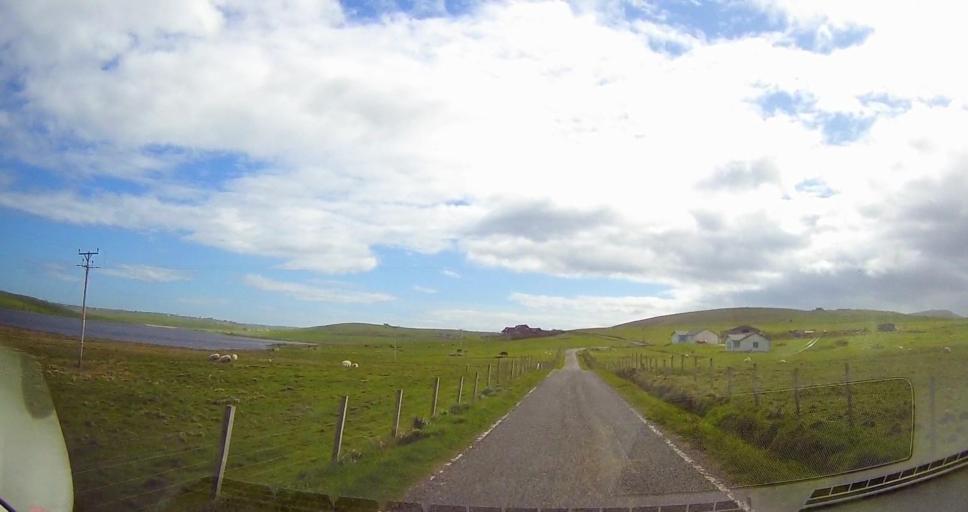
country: GB
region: Scotland
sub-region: Shetland Islands
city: Sandwick
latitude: 59.9354
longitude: -1.3458
